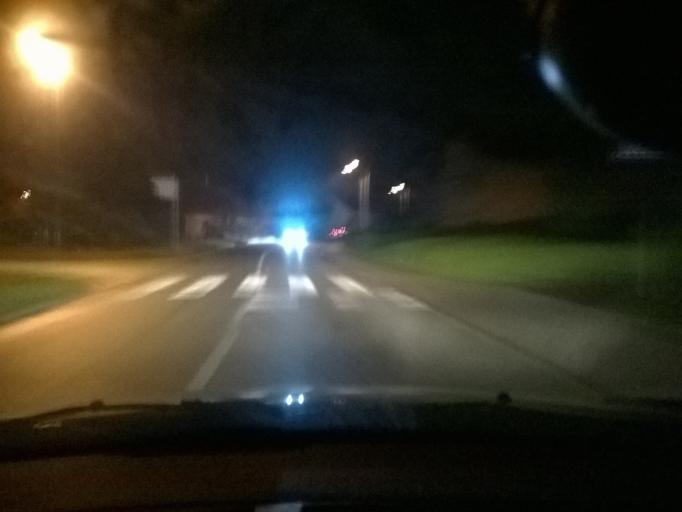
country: HR
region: Krapinsko-Zagorska
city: Zabok
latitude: 46.0373
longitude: 15.9107
